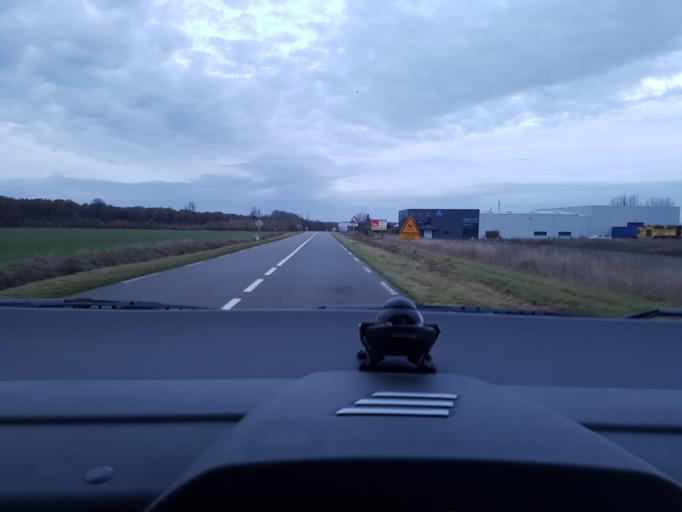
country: FR
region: Picardie
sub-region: Departement de la Somme
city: Poix-de-Picardie
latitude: 49.7626
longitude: 1.9719
